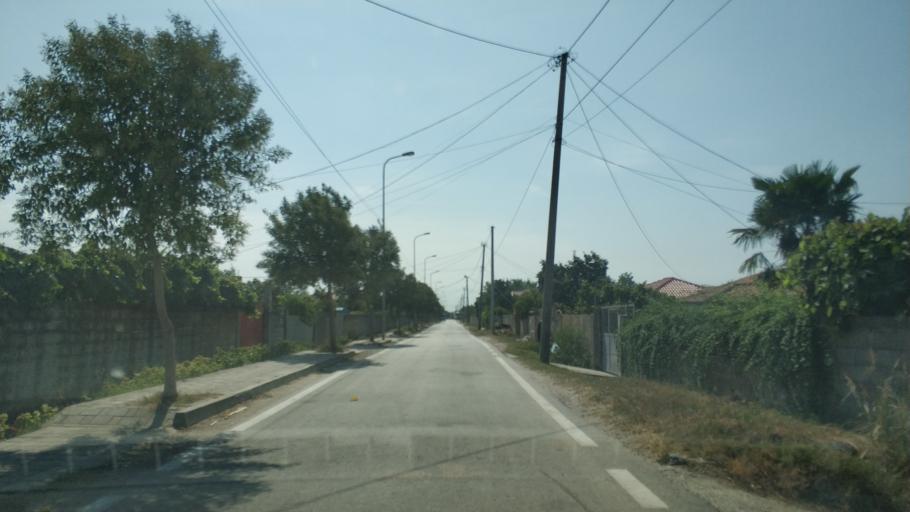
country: AL
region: Fier
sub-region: Rrethi i Fierit
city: Dermenas
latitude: 40.7334
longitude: 19.4719
